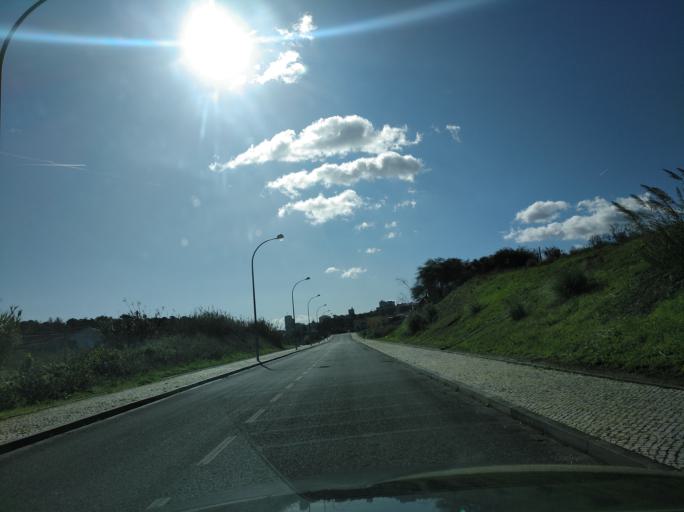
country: PT
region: Lisbon
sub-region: Lisbon
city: Lisbon
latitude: 38.7377
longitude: -9.1187
